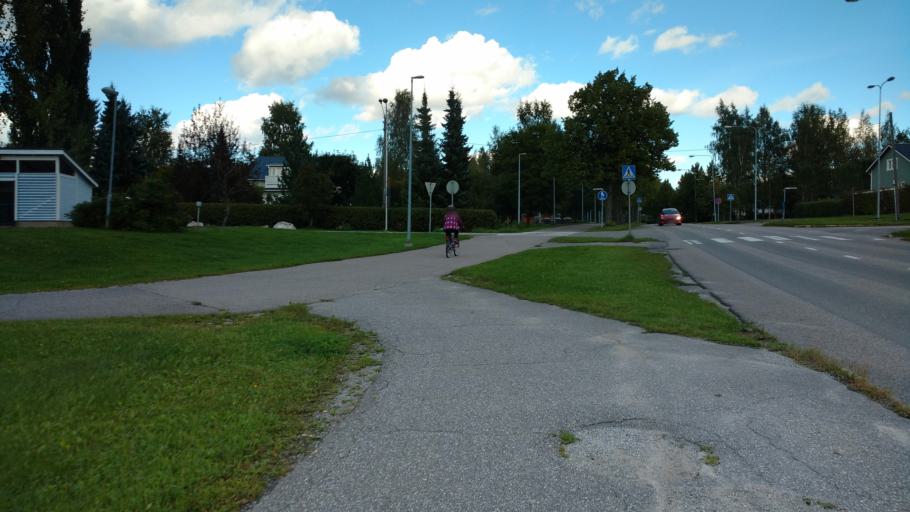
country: FI
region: Varsinais-Suomi
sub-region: Salo
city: Salo
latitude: 60.3817
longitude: 23.1548
